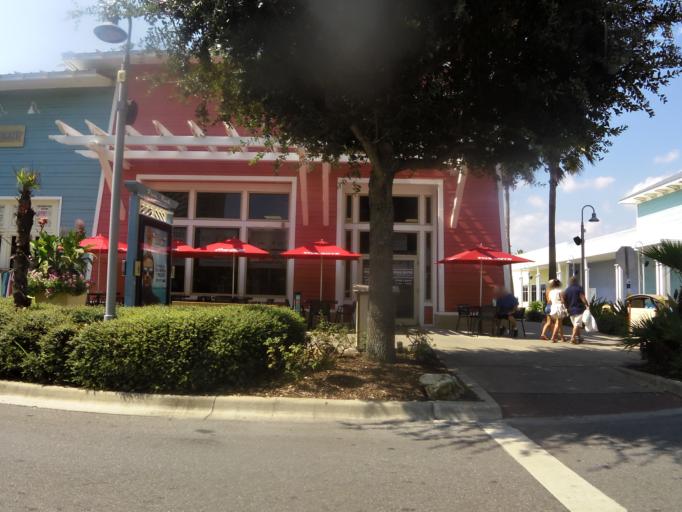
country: US
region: Florida
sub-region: Bay County
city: Laguna Beach
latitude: 30.2175
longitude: -85.8745
